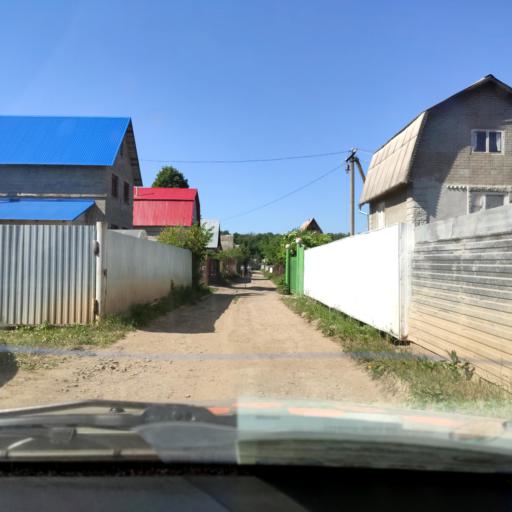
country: RU
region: Bashkortostan
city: Ufa
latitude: 54.7874
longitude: 56.1838
